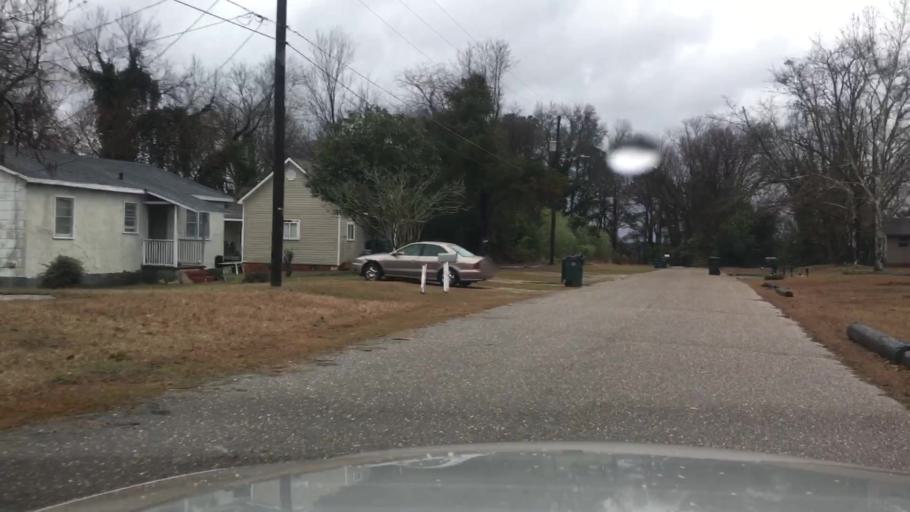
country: US
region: North Carolina
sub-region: Cumberland County
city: Fayetteville
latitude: 35.0309
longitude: -78.8886
